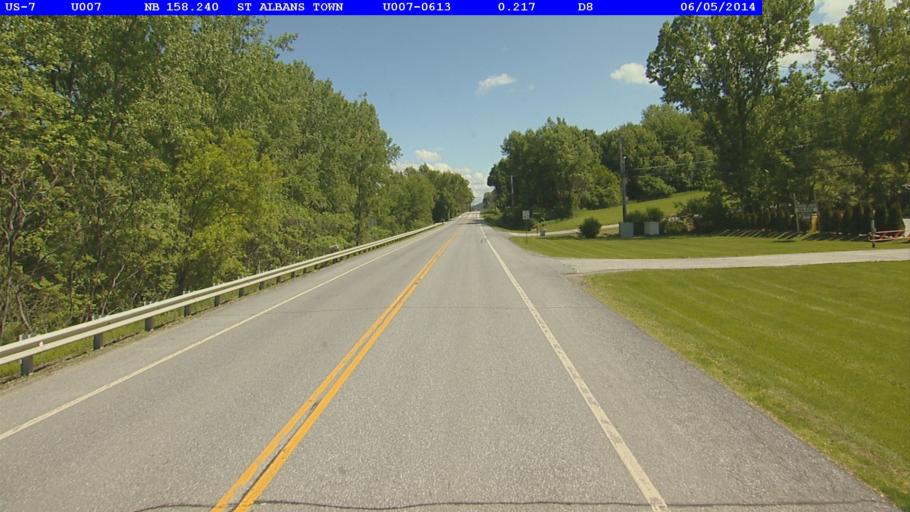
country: US
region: Vermont
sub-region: Franklin County
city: Saint Albans
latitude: 44.7832
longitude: -73.1035
